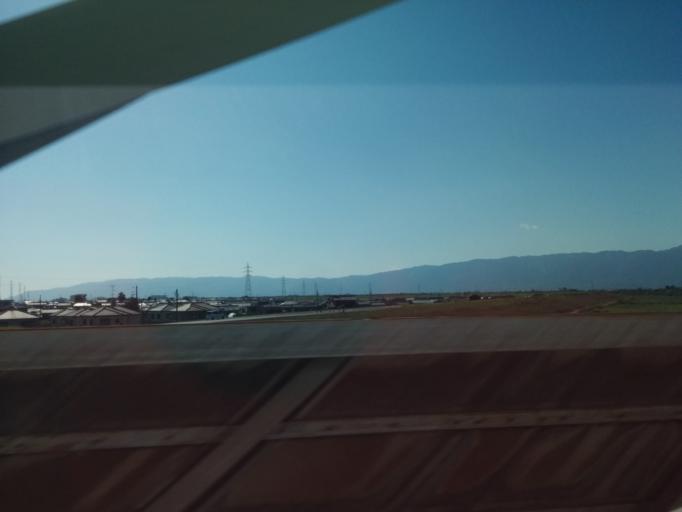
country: JP
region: Gifu
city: Ogaki
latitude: 35.3401
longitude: 136.6515
